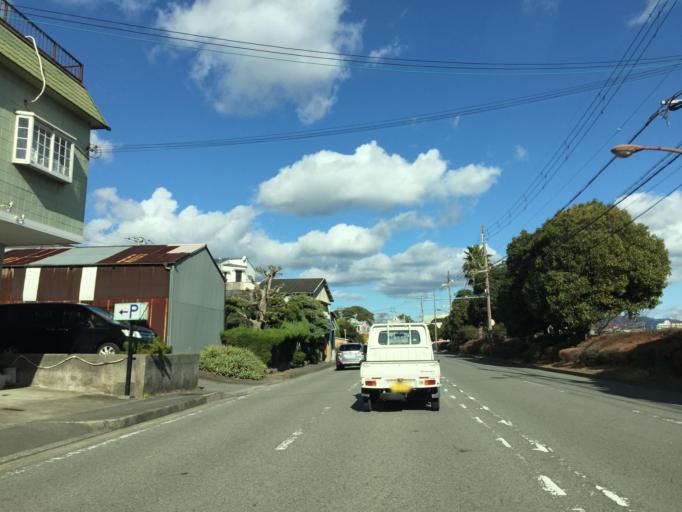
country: JP
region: Wakayama
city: Wakayama-shi
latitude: 34.2135
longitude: 135.1774
